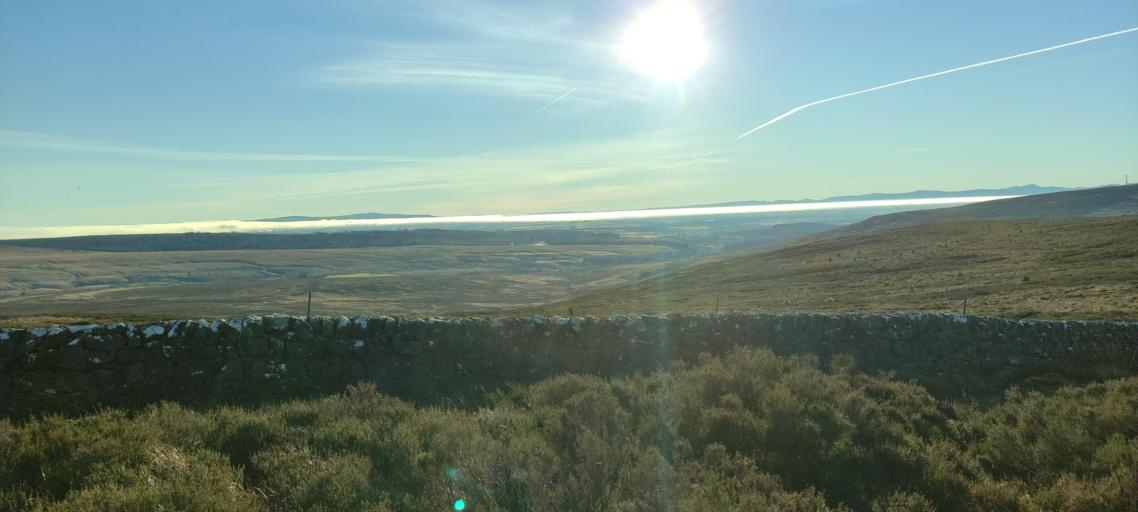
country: GB
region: Scotland
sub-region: Dumfries and Galloway
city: Langholm
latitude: 55.1744
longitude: -2.9633
